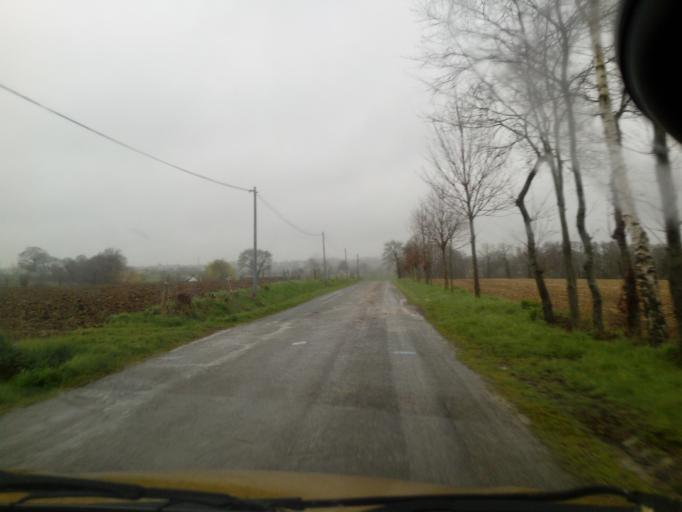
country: FR
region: Brittany
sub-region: Departement d'Ille-et-Vilaine
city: Chevaigne
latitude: 48.2278
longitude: -1.6557
